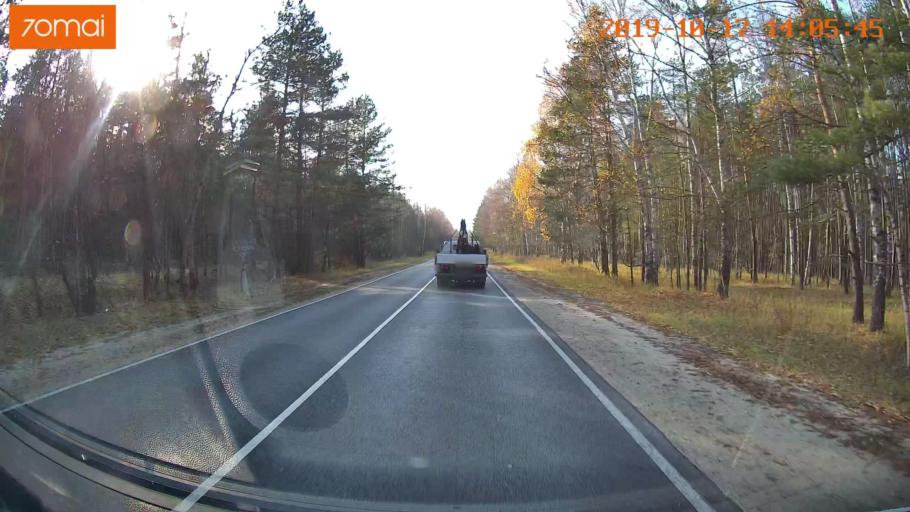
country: RU
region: Rjazan
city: Spas-Klepiki
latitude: 55.1159
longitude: 40.1192
